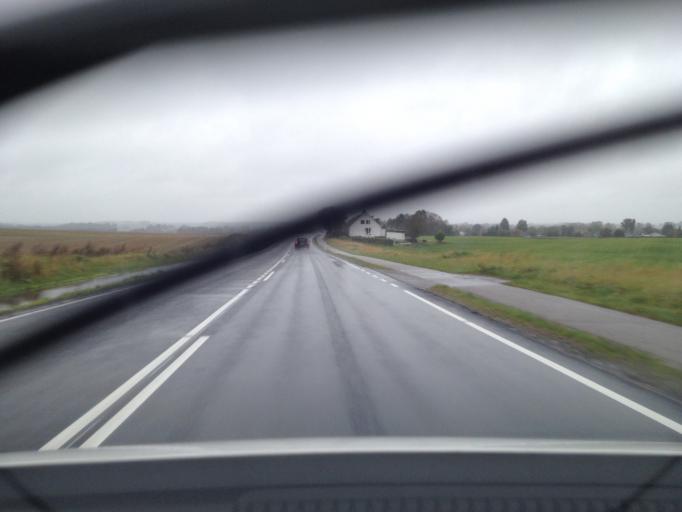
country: DK
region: Zealand
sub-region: Holbaek Kommune
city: Tollose
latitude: 55.5374
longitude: 11.7130
